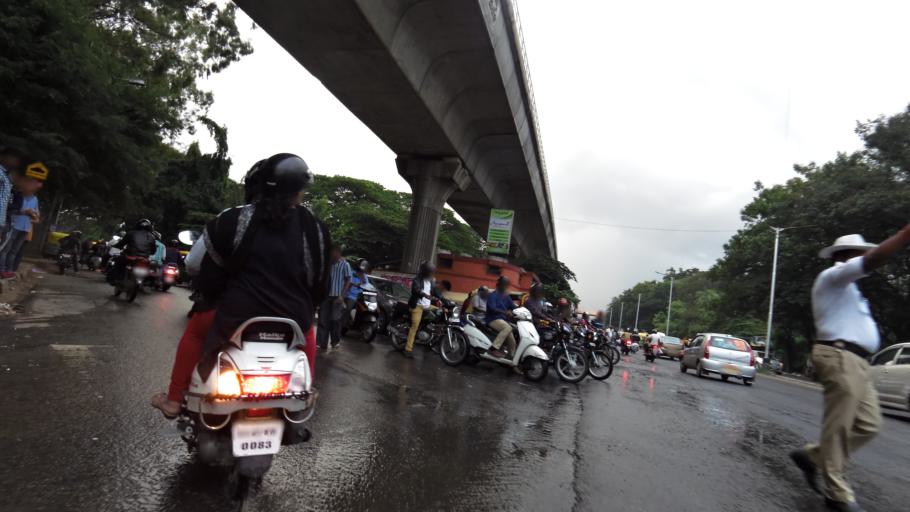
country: IN
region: Karnataka
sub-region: Bangalore Urban
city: Bangalore
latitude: 12.9848
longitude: 77.6423
